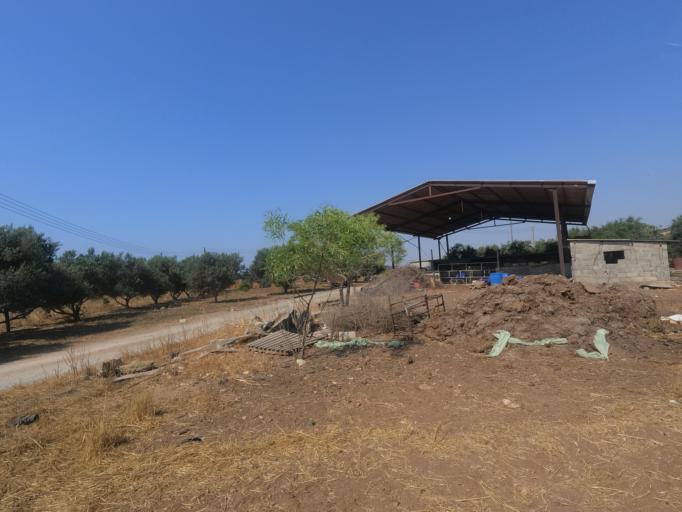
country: CY
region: Ammochostos
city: Avgorou
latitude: 35.0172
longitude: 33.8216
